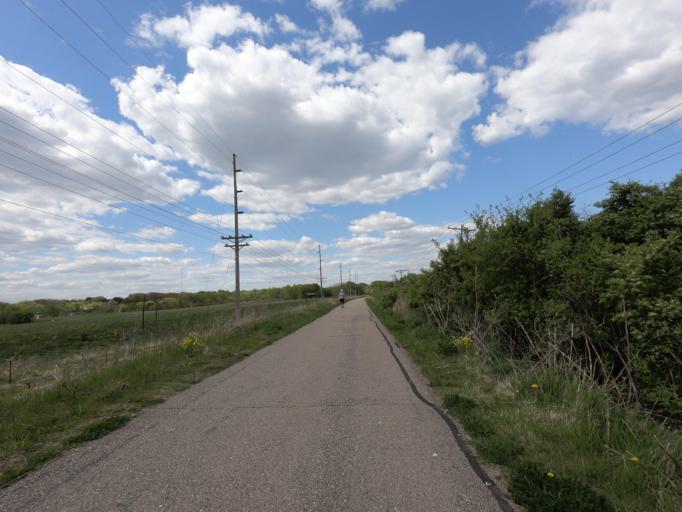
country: US
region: Wisconsin
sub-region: Dane County
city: Fitchburg
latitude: 43.0186
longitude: -89.4615
